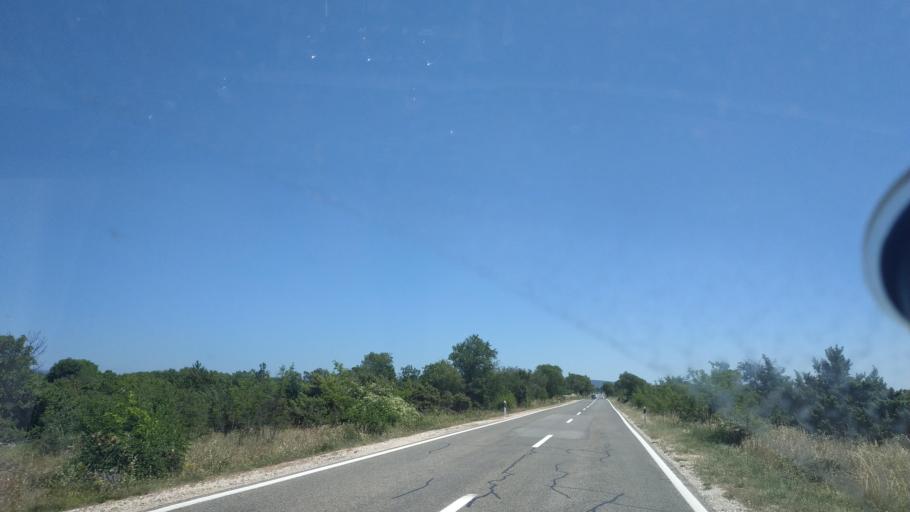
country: HR
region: Sibensko-Kniniska
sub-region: Grad Sibenik
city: Sibenik
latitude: 43.7823
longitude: 16.0016
